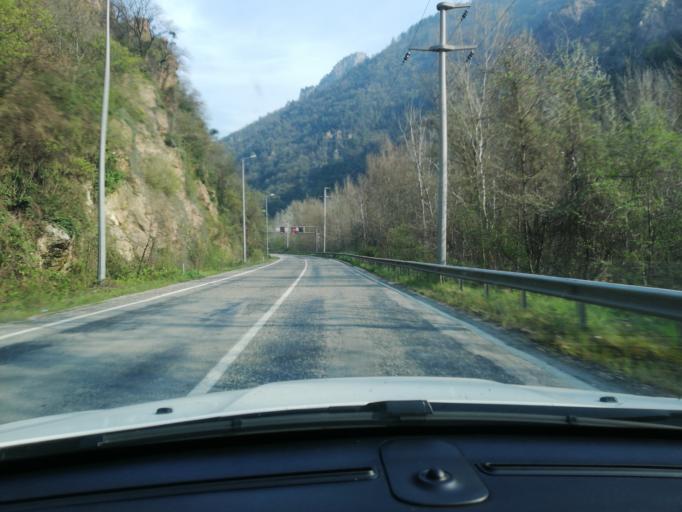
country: TR
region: Karabuk
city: Yenice
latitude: 41.1802
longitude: 32.4482
